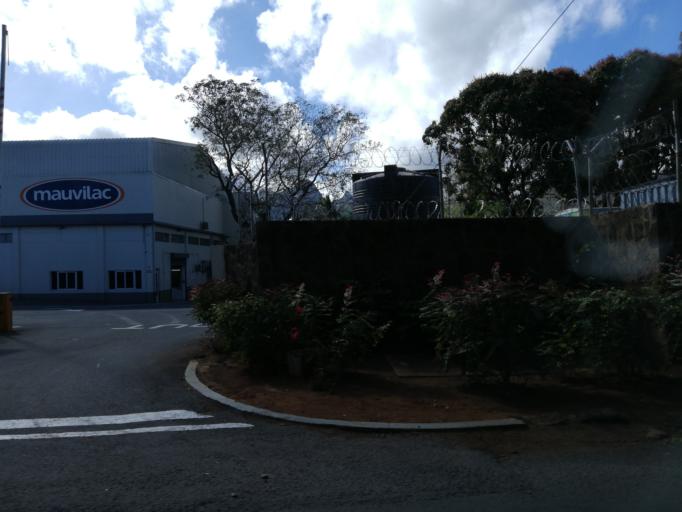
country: MU
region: Moka
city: Pailles
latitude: -20.1876
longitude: 57.4783
